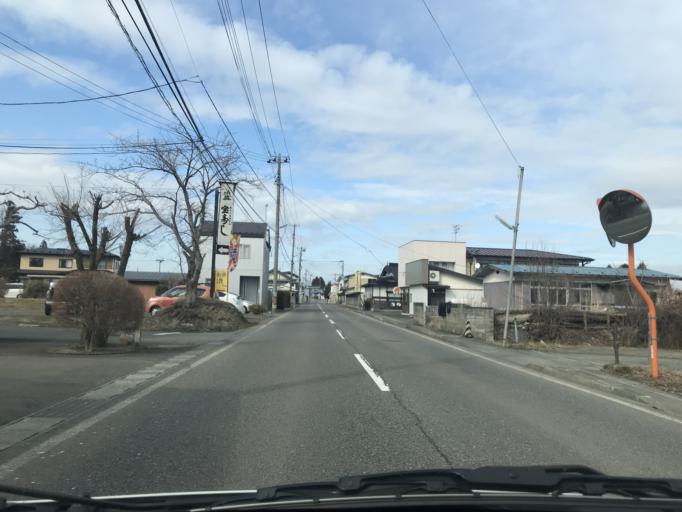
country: JP
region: Iwate
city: Hanamaki
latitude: 39.3587
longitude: 141.0504
